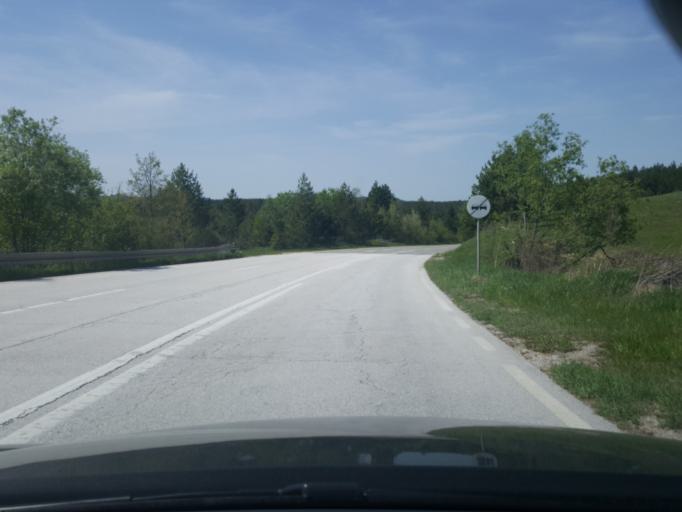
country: RS
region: Central Serbia
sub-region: Zlatiborski Okrug
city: Cajetina
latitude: 43.8257
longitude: 19.6412
